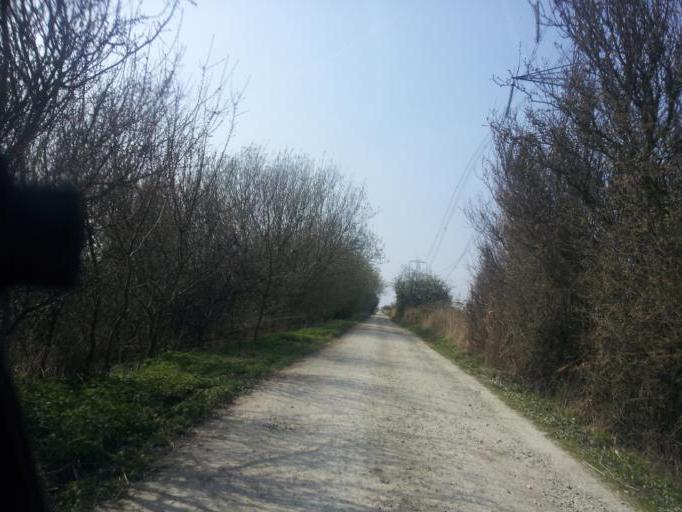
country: GB
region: England
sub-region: Kent
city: Gravesend
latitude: 51.4377
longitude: 0.4288
